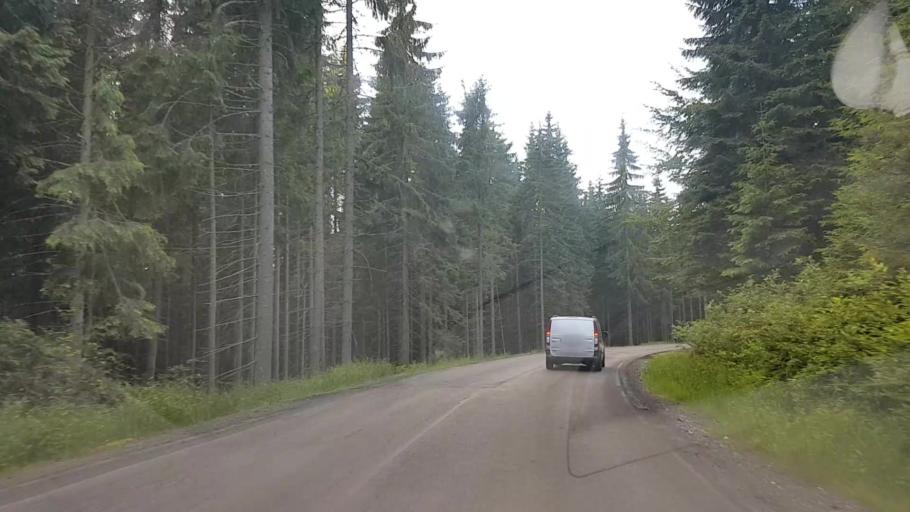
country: RO
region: Harghita
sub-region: Comuna Varsag
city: Varsag
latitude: 46.6604
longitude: 25.3016
